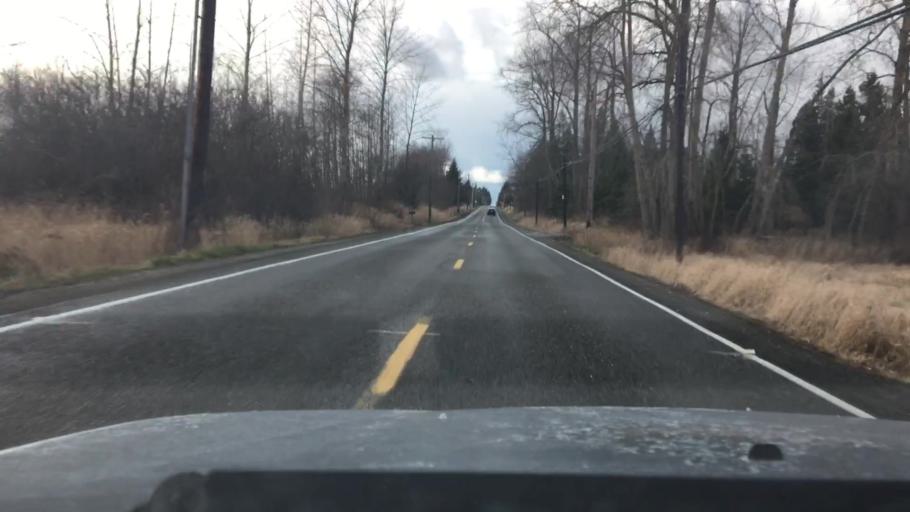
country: US
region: Washington
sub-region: Whatcom County
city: Ferndale
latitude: 48.8484
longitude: -122.6545
